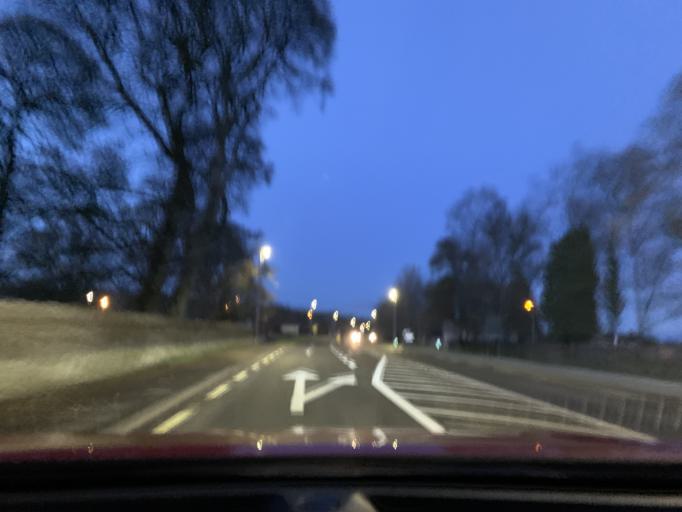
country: IE
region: Connaught
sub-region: Roscommon
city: Boyle
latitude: 53.9792
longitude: -8.2977
